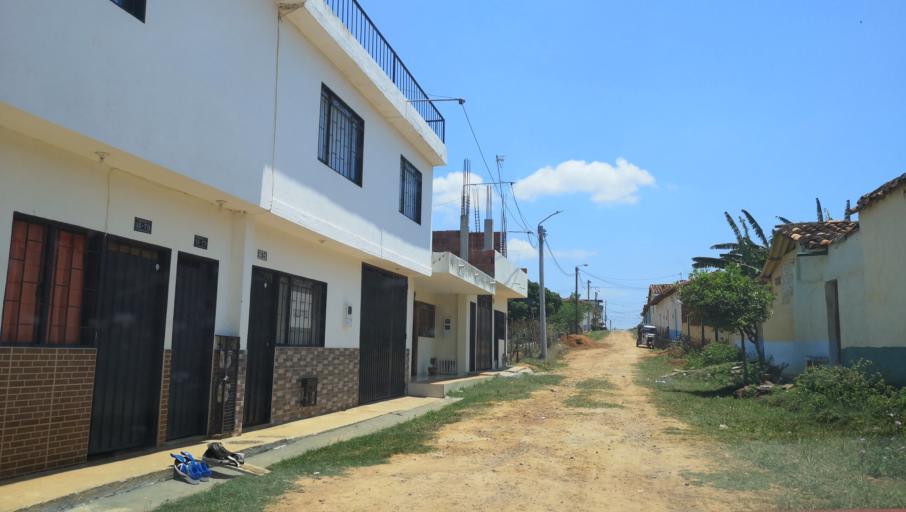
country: CO
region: Santander
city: Villanueva
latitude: 6.6731
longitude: -73.1717
